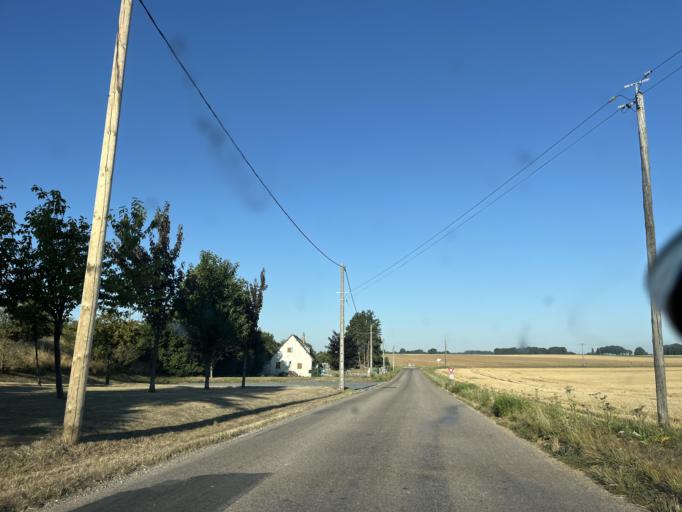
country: FR
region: Haute-Normandie
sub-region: Departement de la Seine-Maritime
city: Fauville-en-Caux
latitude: 49.6085
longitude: 0.5962
